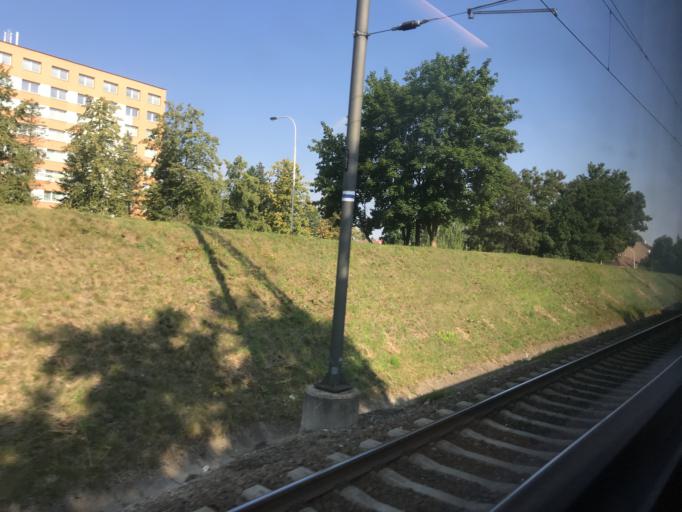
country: CZ
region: Jihocesky
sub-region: Okres Tabor
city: Sezimovo Usti
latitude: 49.4050
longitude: 14.6825
